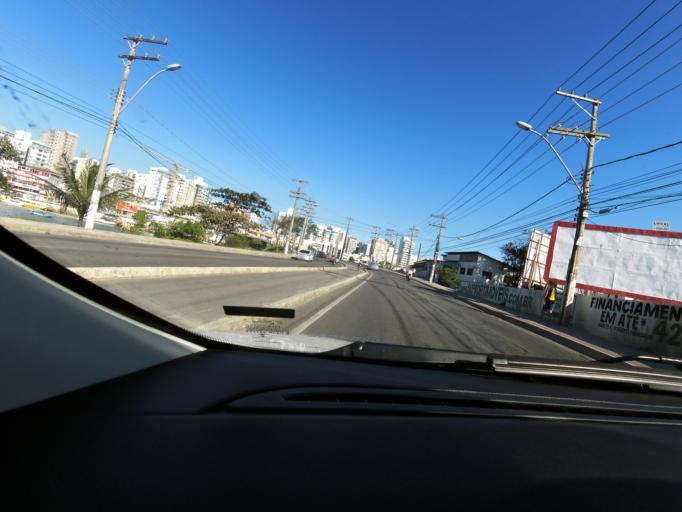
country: BR
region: Espirito Santo
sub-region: Guarapari
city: Guarapari
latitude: -20.6672
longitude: -40.5003
